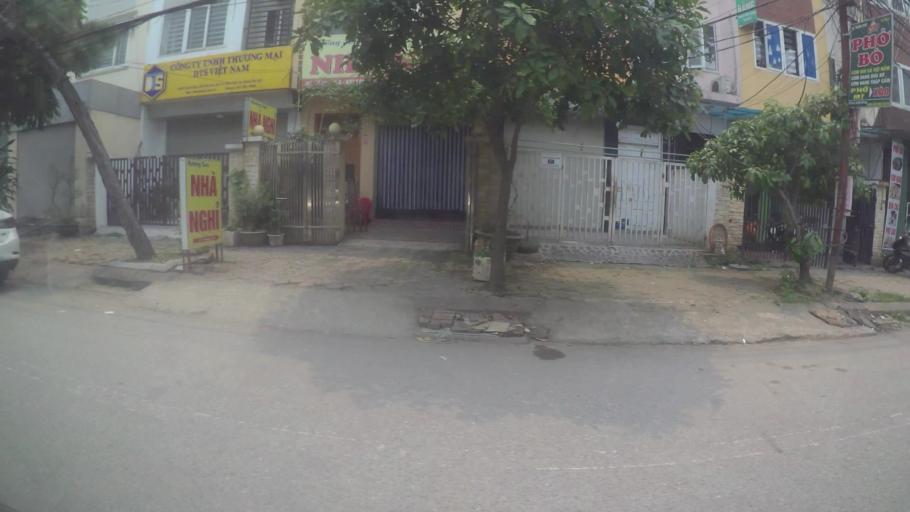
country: VN
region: Ha Noi
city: Ha Dong
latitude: 20.9747
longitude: 105.7645
